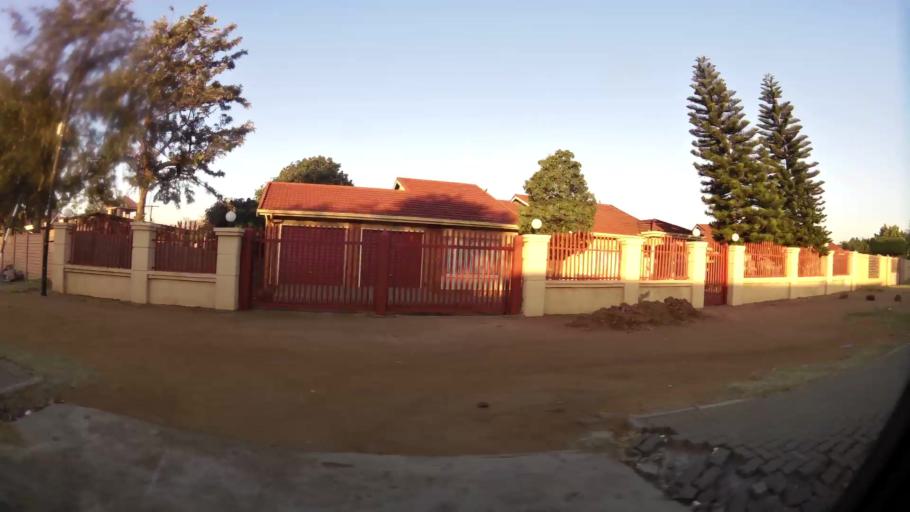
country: ZA
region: North-West
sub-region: Bojanala Platinum District Municipality
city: Rustenburg
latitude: -25.6401
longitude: 27.2089
